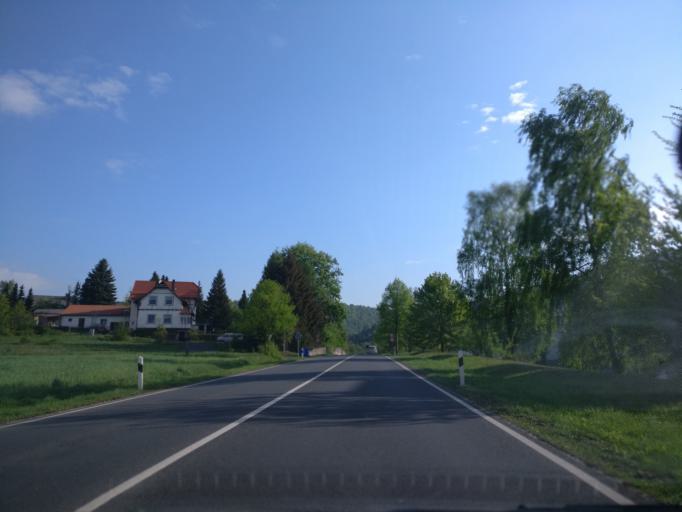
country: DE
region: Lower Saxony
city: Hannoversch Munden
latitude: 51.4406
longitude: 9.6609
